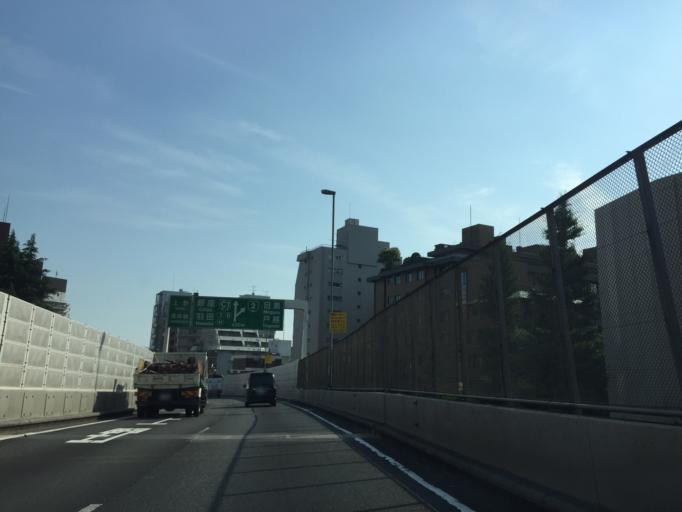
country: JP
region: Tokyo
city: Tokyo
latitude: 35.6604
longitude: 139.7373
